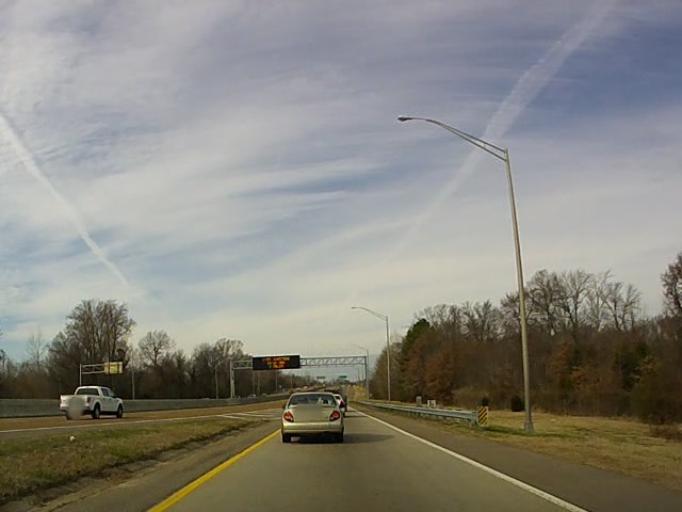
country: US
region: Tennessee
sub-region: Shelby County
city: Germantown
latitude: 35.0689
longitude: -89.8488
